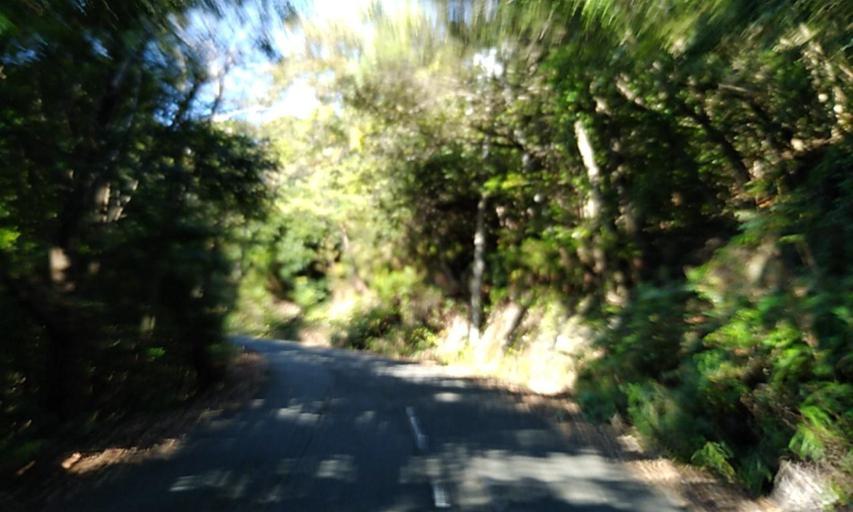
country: JP
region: Shizuoka
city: Hamakita
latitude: 34.8167
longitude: 137.6436
